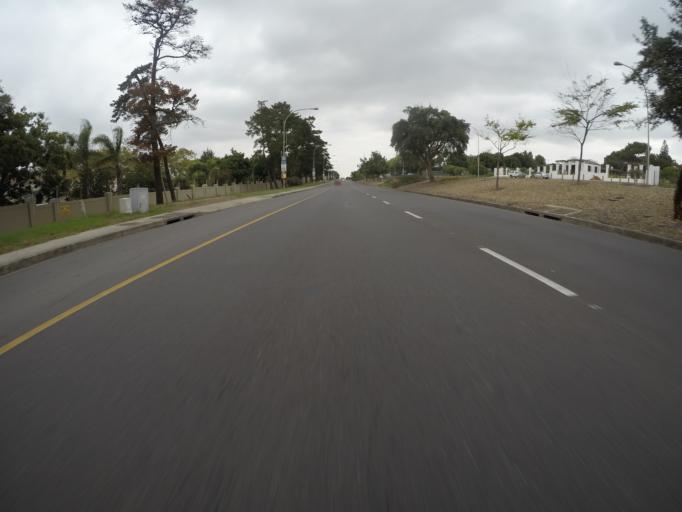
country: ZA
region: Western Cape
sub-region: City of Cape Town
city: Kraaifontein
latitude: -33.8500
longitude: 18.6442
